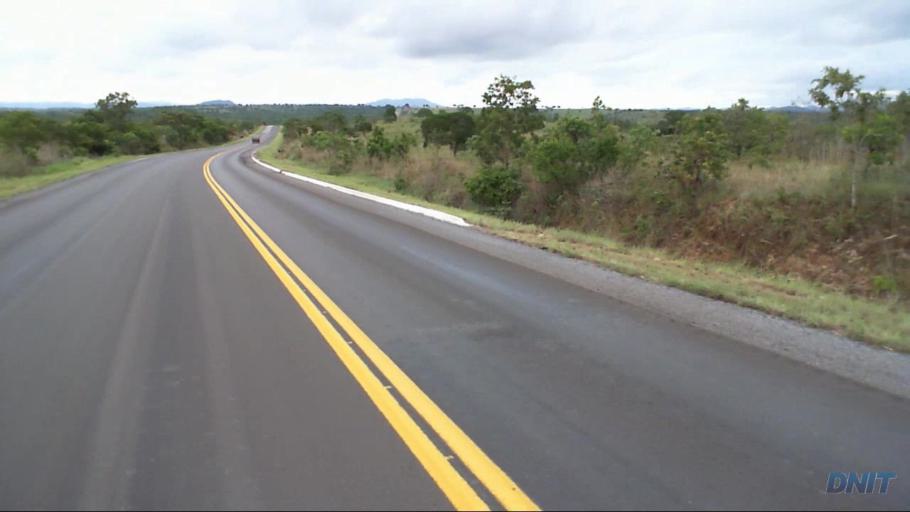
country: BR
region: Goias
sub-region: Padre Bernardo
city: Padre Bernardo
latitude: -15.2119
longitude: -48.5717
